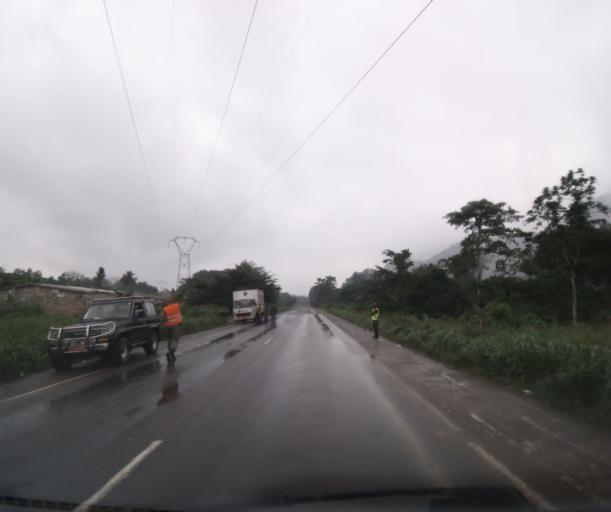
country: CM
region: Centre
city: Eseka
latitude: 3.8917
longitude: 10.7717
